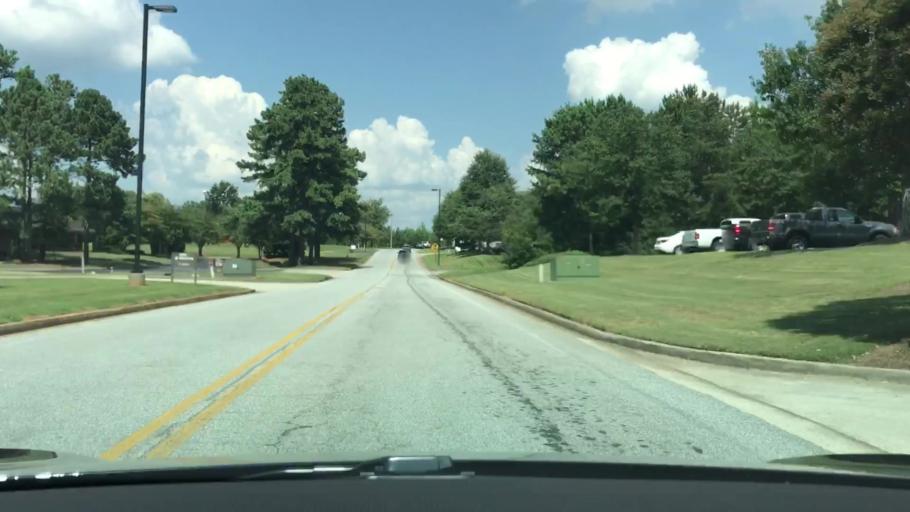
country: US
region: Georgia
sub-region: Gwinnett County
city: Buford
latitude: 34.1012
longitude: -84.0036
